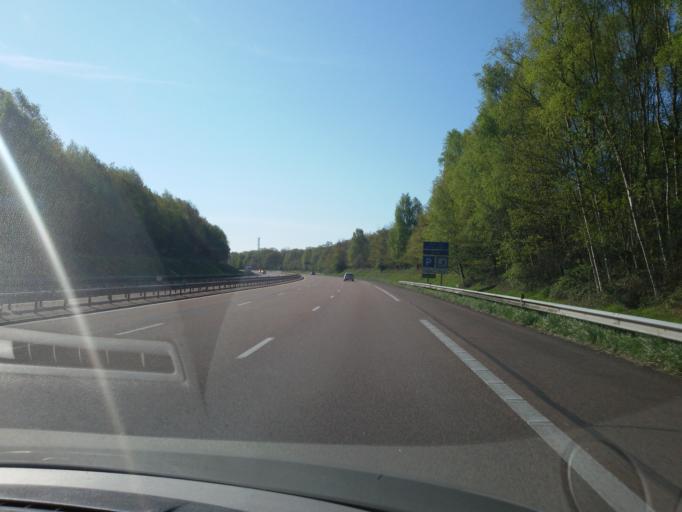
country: FR
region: Bourgogne
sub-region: Departement de l'Yonne
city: Aillant-sur-Tholon
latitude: 47.9162
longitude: 3.2890
